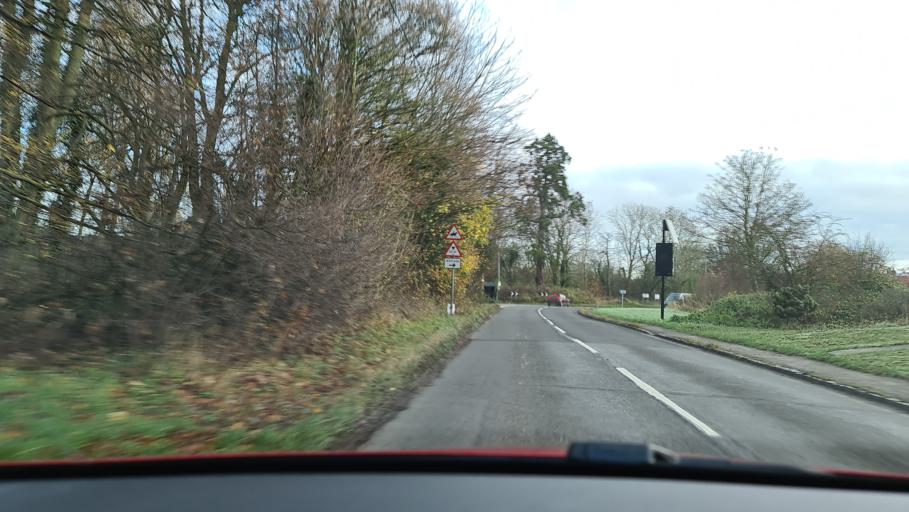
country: GB
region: England
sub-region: Oxfordshire
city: Chinnor
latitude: 51.7204
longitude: -0.8758
